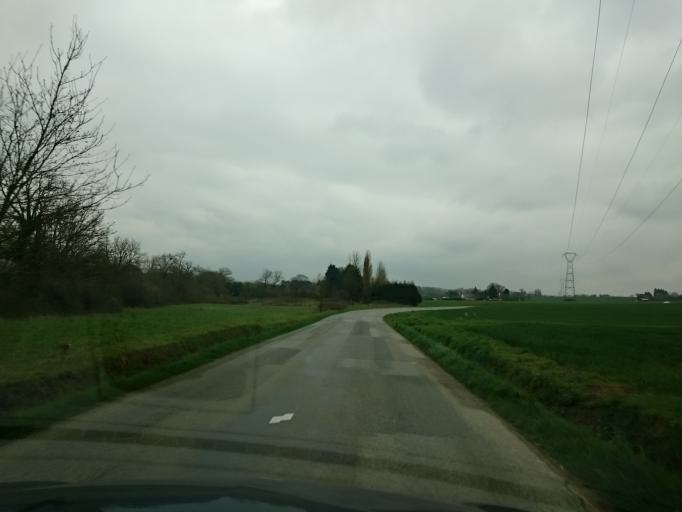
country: FR
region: Brittany
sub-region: Departement d'Ille-et-Vilaine
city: Chanteloup
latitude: 47.9692
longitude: -1.6025
